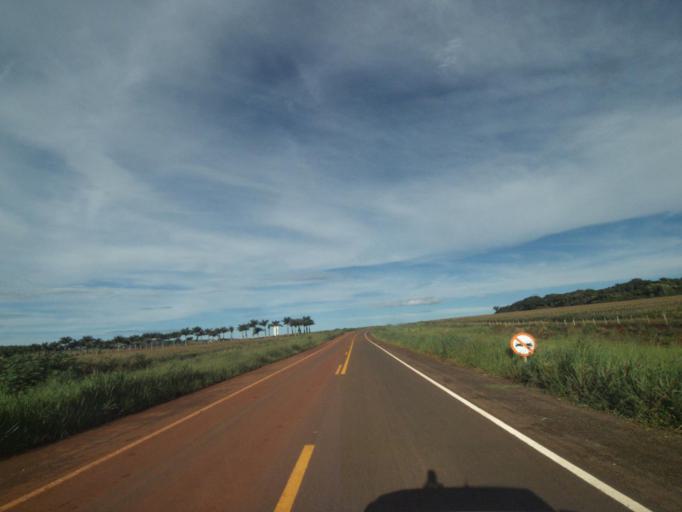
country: BR
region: Goias
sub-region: Jaragua
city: Jaragua
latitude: -15.9029
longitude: -49.5406
